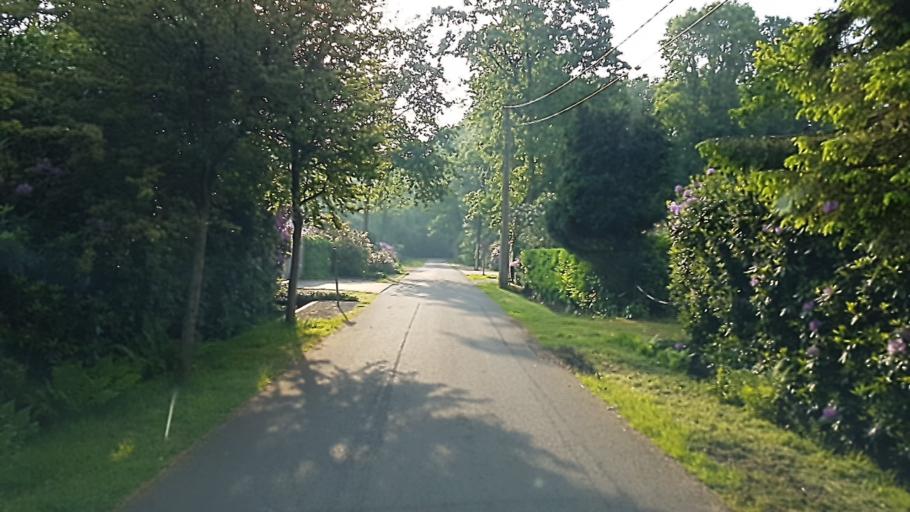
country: BE
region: Flanders
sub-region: Provincie Antwerpen
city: Zoersel
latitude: 51.2716
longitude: 4.6628
